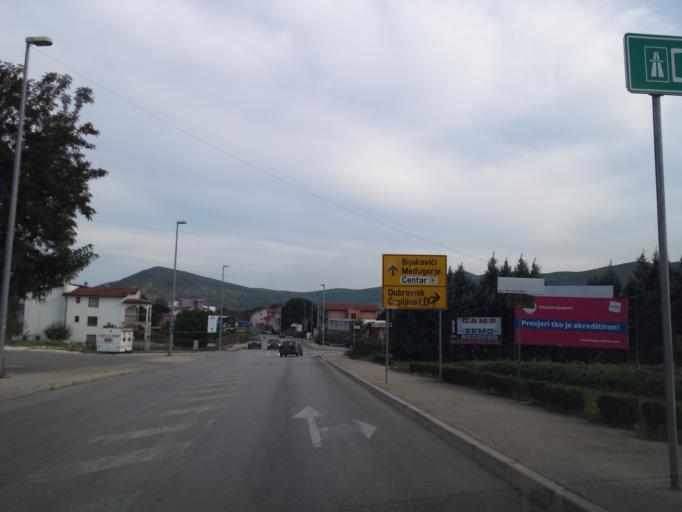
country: BA
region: Federation of Bosnia and Herzegovina
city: Citluk
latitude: 43.1984
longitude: 17.6724
